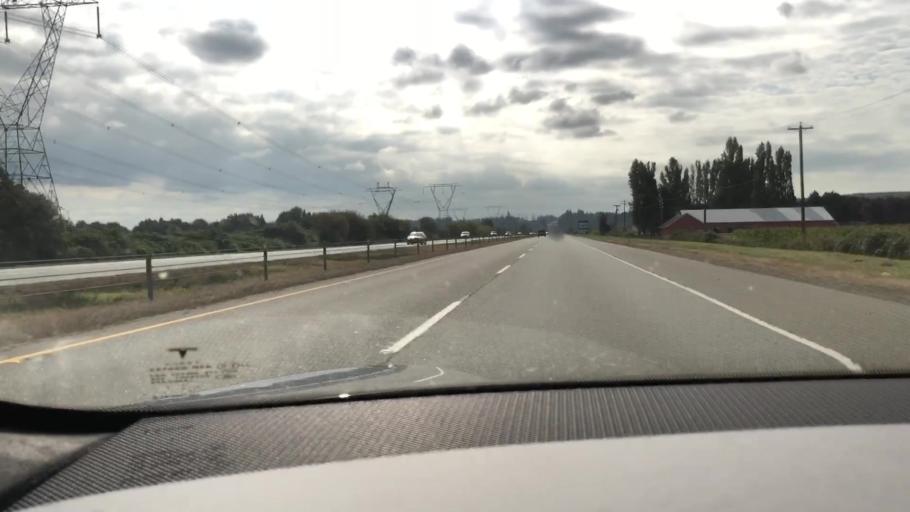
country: CA
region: British Columbia
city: Surrey
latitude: 49.0842
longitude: -122.8368
